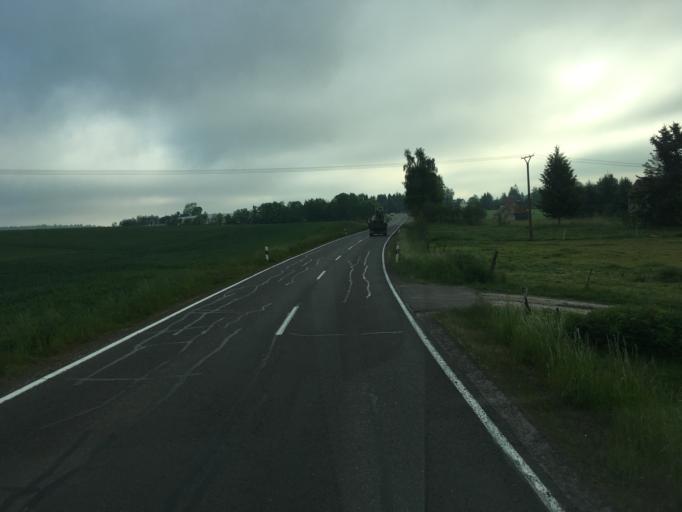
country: DE
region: Saxony
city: Hainichen
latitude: 50.9797
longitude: 13.1027
